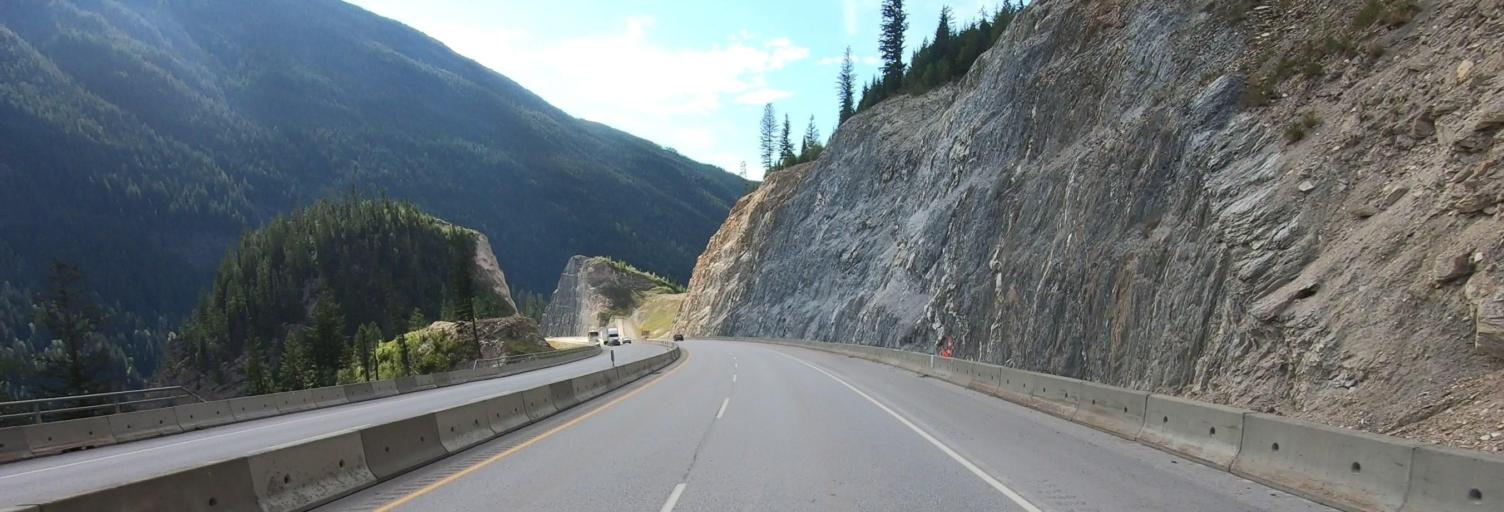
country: CA
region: British Columbia
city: Golden
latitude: 51.2820
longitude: -116.7922
